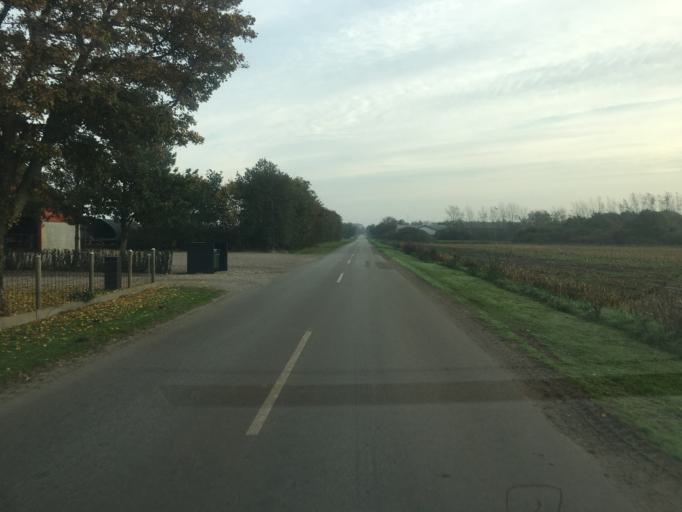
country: DK
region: South Denmark
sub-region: Tonder Kommune
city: Logumkloster
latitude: 55.0803
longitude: 9.0146
